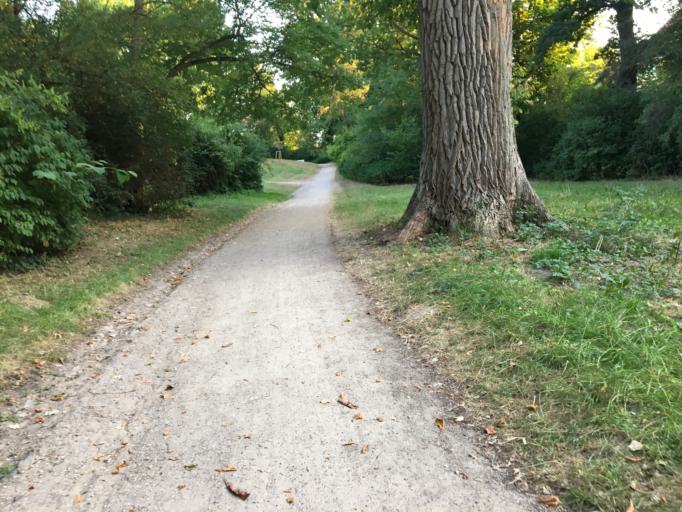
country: DE
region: Schleswig-Holstein
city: Eutin
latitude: 54.1342
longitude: 10.6203
